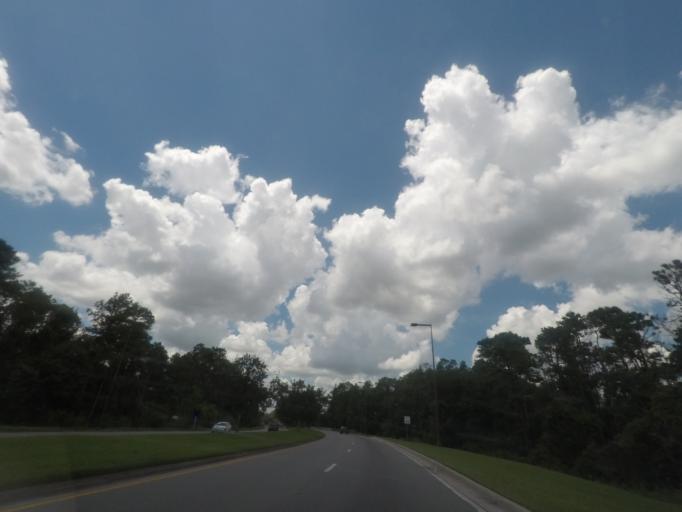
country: US
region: Florida
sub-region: Osceola County
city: Celebration
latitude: 28.3635
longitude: -81.5673
